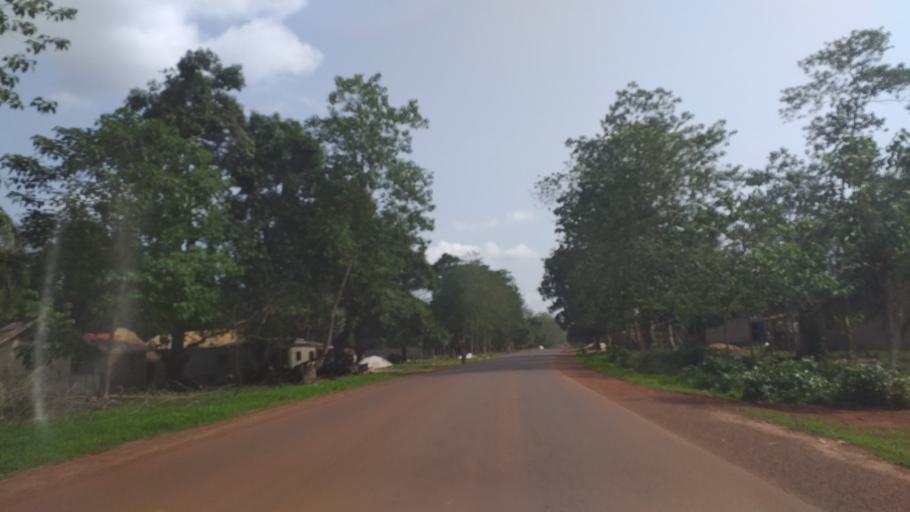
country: GN
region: Boke
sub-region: Boke Prefecture
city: Sangueya
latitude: 10.8220
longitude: -14.3735
